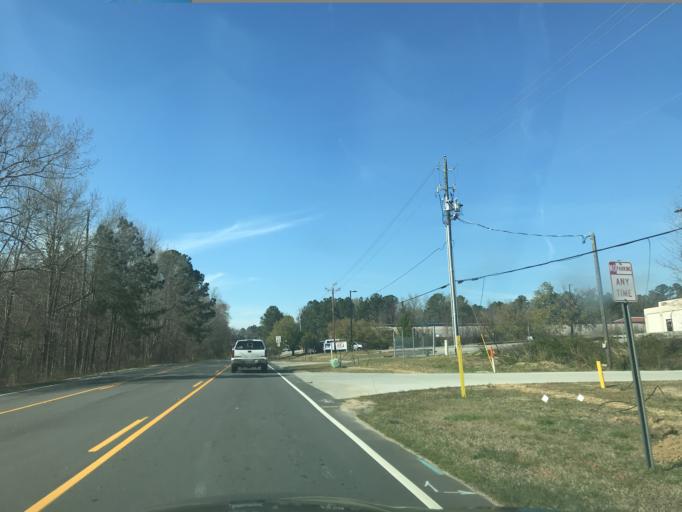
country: US
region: North Carolina
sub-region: Wake County
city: Fuquay-Varina
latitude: 35.5919
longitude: -78.7580
